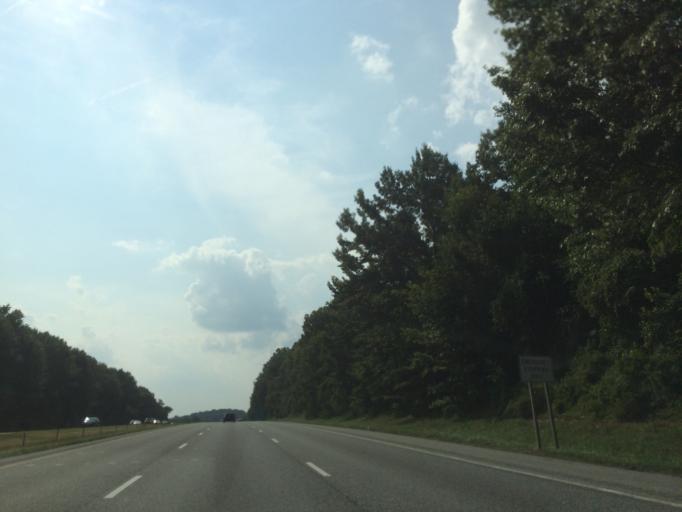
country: US
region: Maryland
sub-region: Carroll County
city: Sykesville
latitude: 39.3078
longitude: -76.9408
